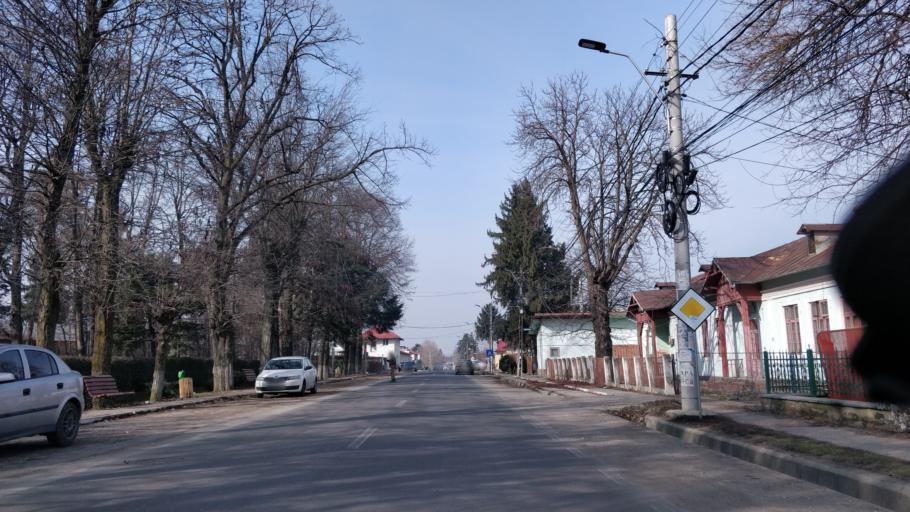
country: RO
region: Giurgiu
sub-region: Comuna Bolintin Deal
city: Bolintin Deal
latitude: 44.4536
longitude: 25.8235
